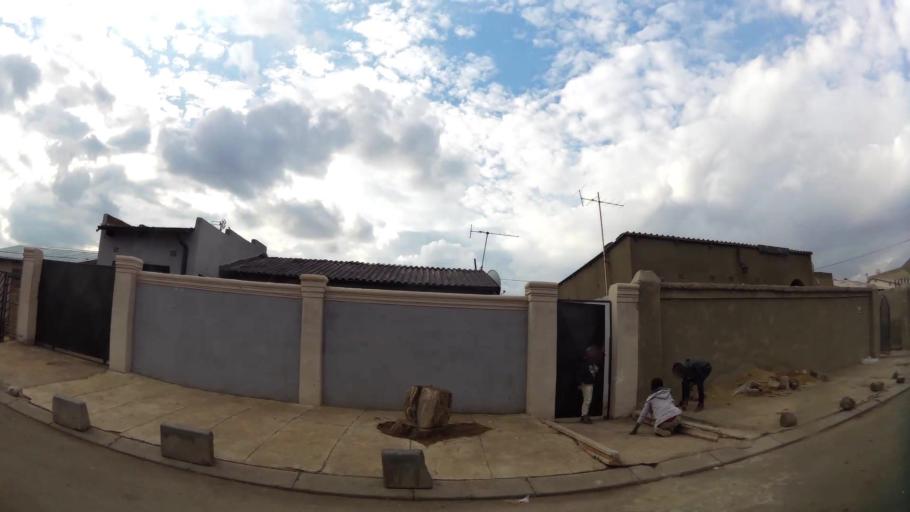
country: ZA
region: Gauteng
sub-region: City of Johannesburg Metropolitan Municipality
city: Soweto
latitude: -26.2466
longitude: 27.8137
